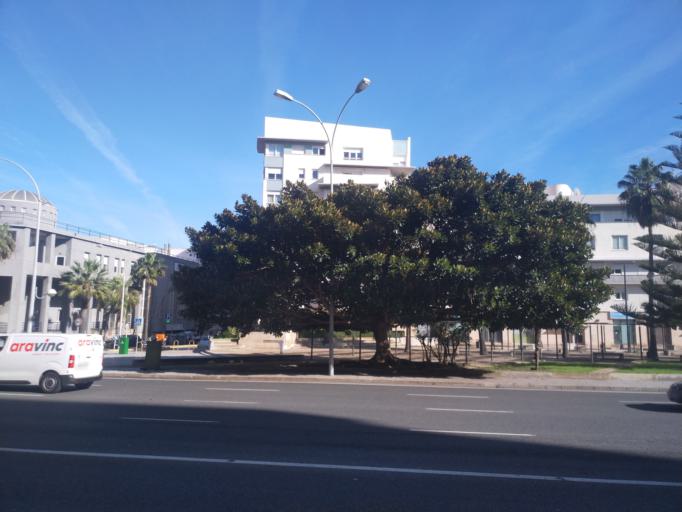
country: ES
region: Andalusia
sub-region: Provincia de Cadiz
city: Cadiz
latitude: 36.4969
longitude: -6.2714
